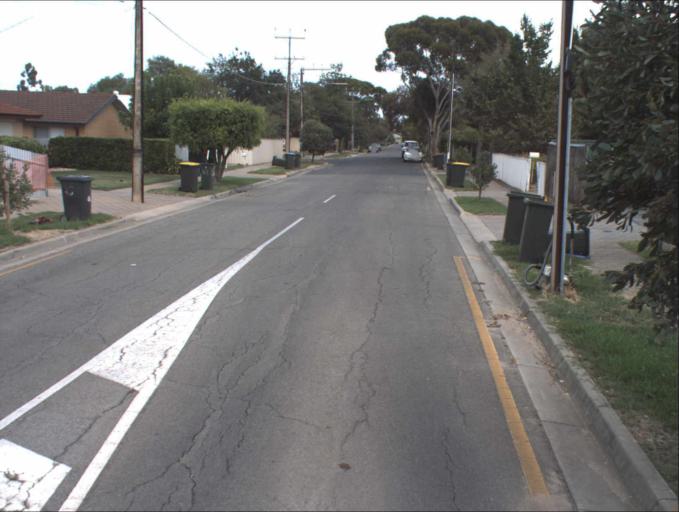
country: AU
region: South Australia
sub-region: Campbelltown
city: Paradise
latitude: -34.8583
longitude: 138.6669
